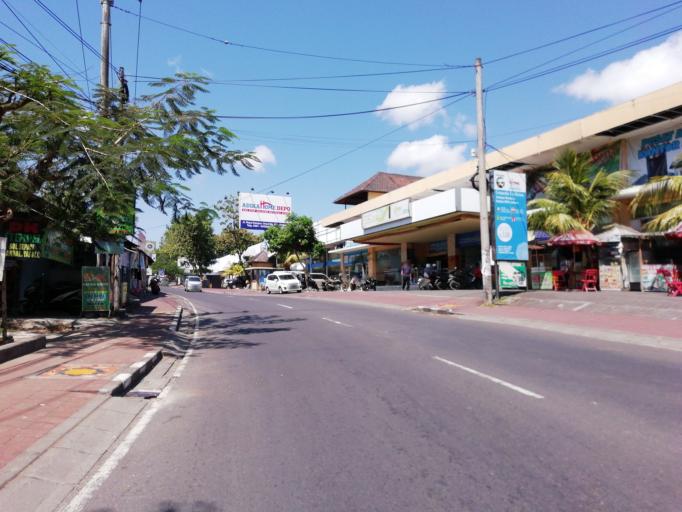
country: ID
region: Bali
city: Jimbaran
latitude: -8.7893
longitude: 115.1772
